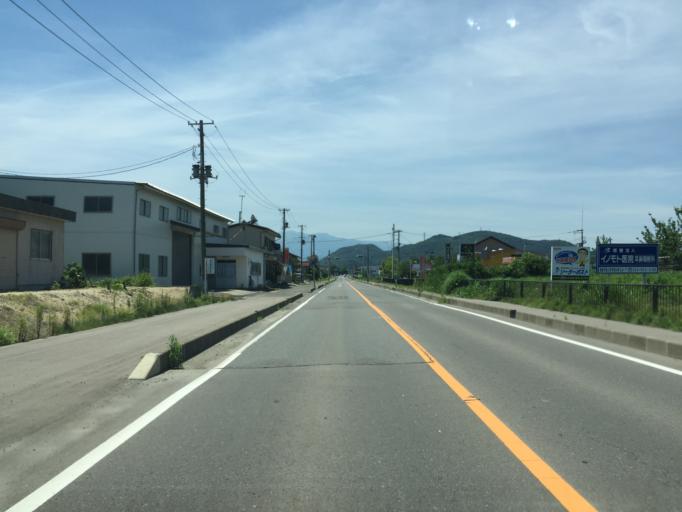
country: JP
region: Fukushima
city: Fukushima-shi
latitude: 37.7721
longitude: 140.5066
